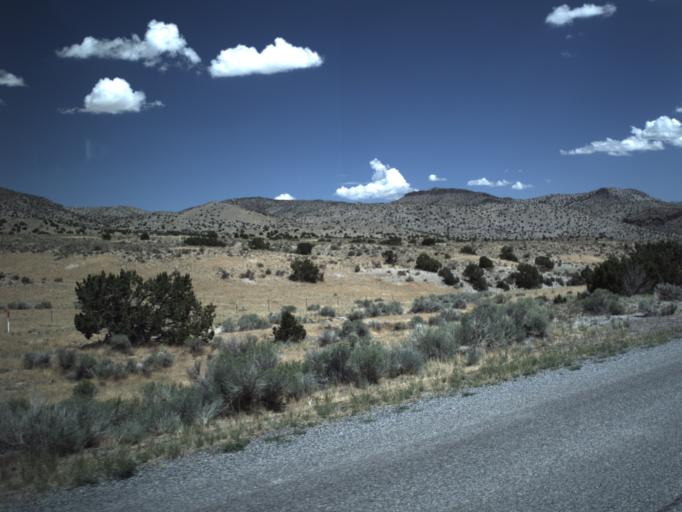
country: US
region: Utah
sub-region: Beaver County
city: Milford
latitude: 39.0763
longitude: -113.6284
